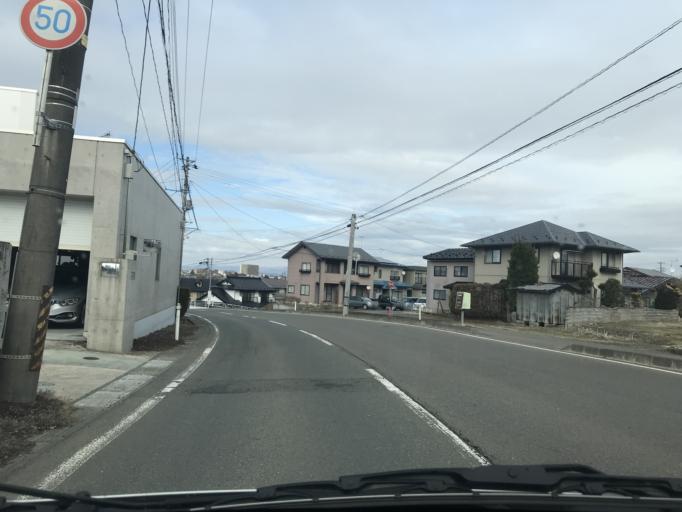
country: JP
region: Iwate
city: Hanamaki
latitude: 39.3765
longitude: 141.1064
